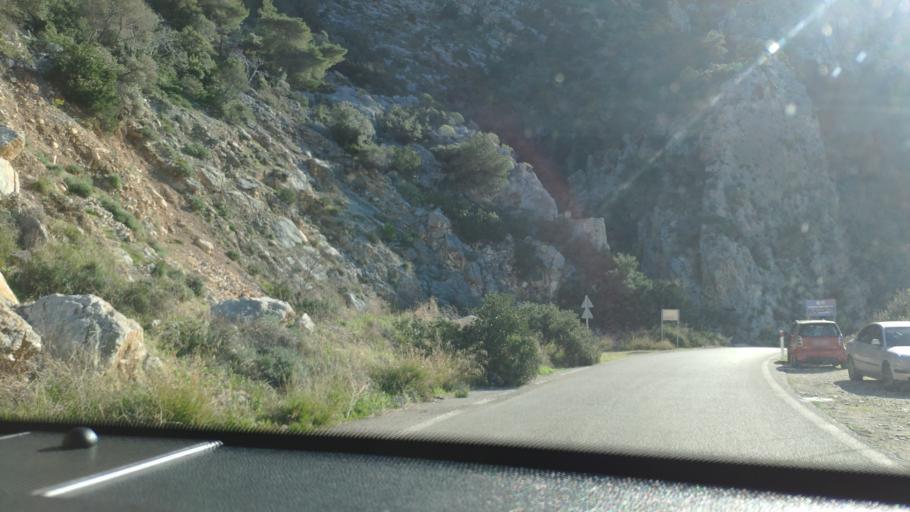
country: GR
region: Attica
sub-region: Nomarchia Dytikis Attikis
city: Kineta
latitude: 38.0618
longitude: 23.1205
